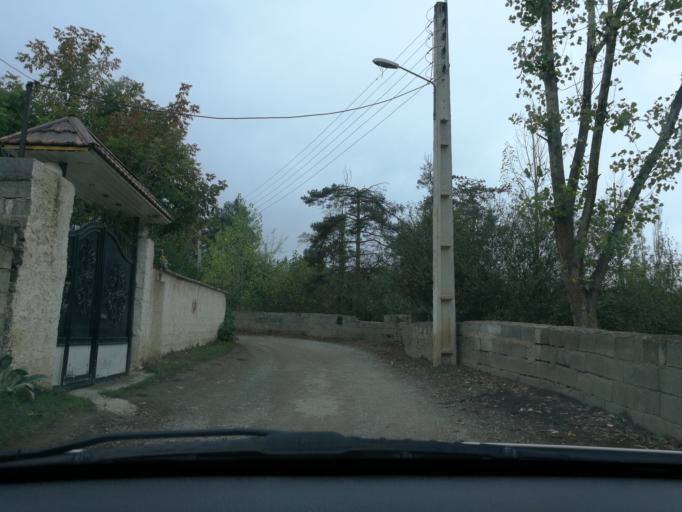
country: IR
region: Mazandaran
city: `Abbasabad
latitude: 36.5064
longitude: 51.1989
